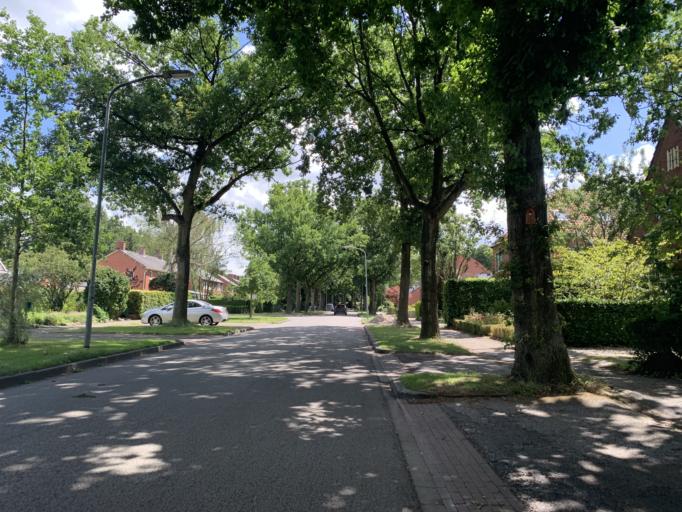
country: NL
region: Groningen
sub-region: Gemeente Haren
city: Haren
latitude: 53.1660
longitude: 6.6150
